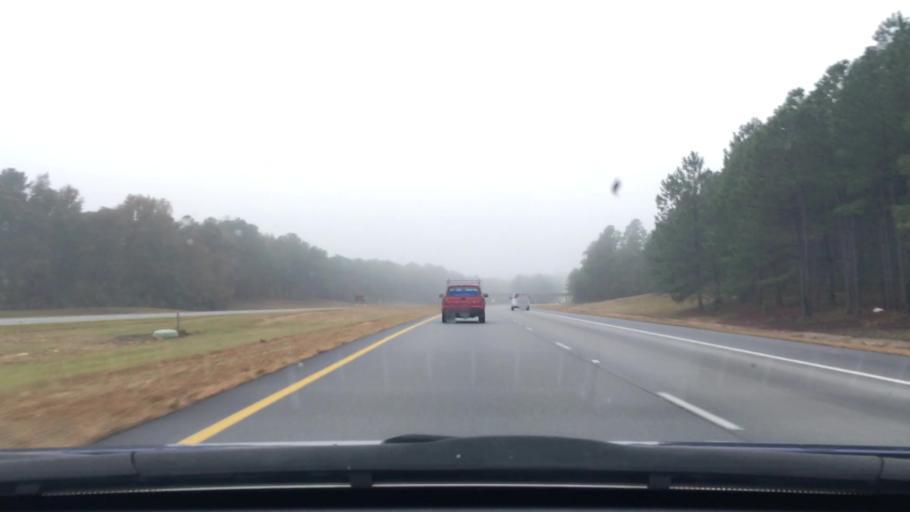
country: US
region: South Carolina
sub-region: Kershaw County
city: Camden
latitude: 34.2082
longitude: -80.4476
